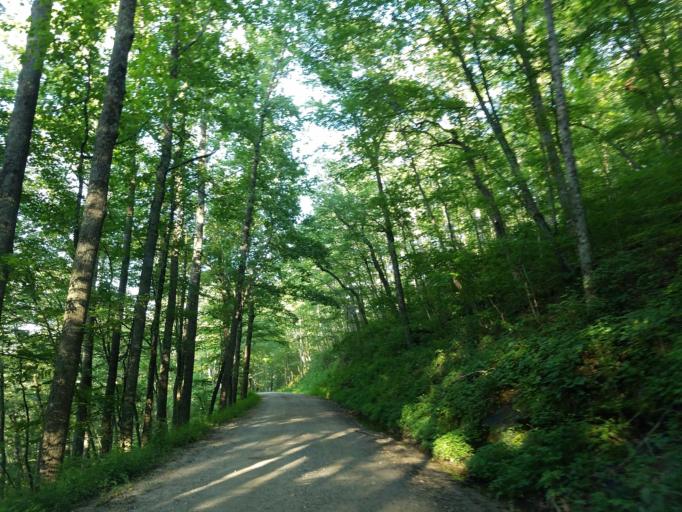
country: US
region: Georgia
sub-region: Lumpkin County
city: Dahlonega
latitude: 34.6568
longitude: -84.0915
